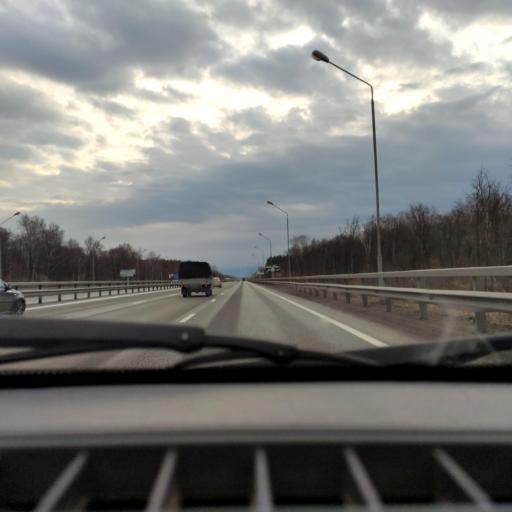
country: RU
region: Bashkortostan
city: Avdon
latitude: 54.6723
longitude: 55.8272
